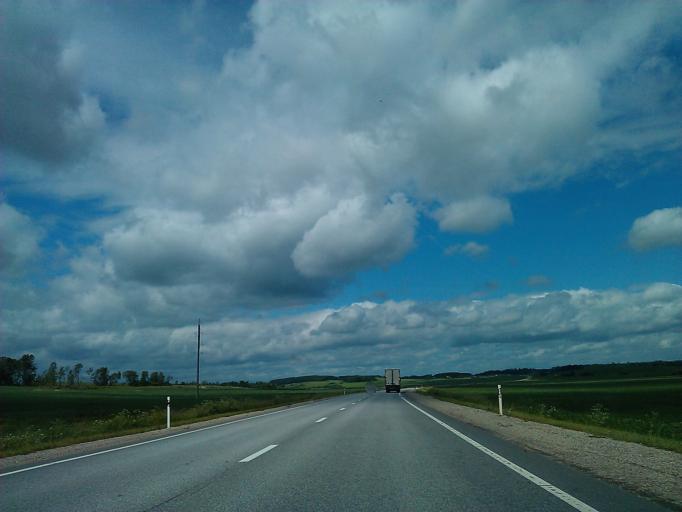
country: LV
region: Tukuma Rajons
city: Tukums
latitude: 56.9576
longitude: 23.0799
